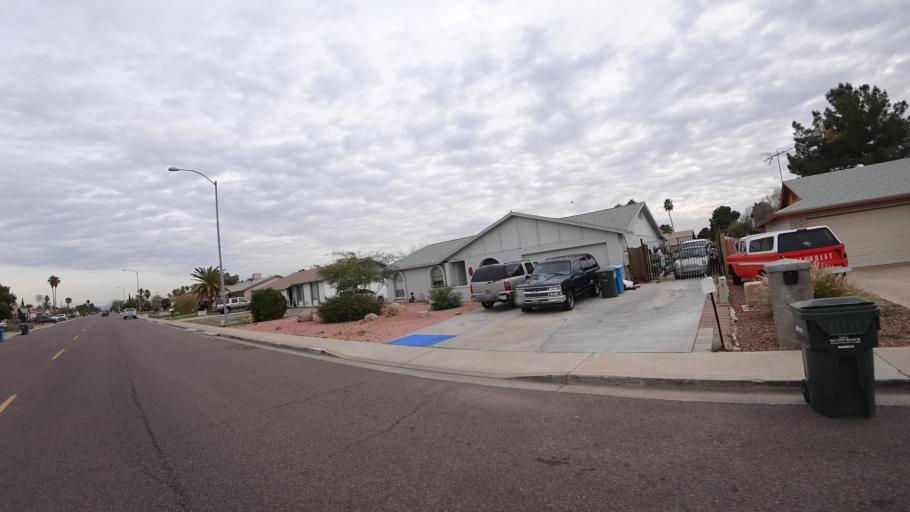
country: US
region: Arizona
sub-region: Maricopa County
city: Peoria
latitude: 33.6473
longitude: -112.1401
